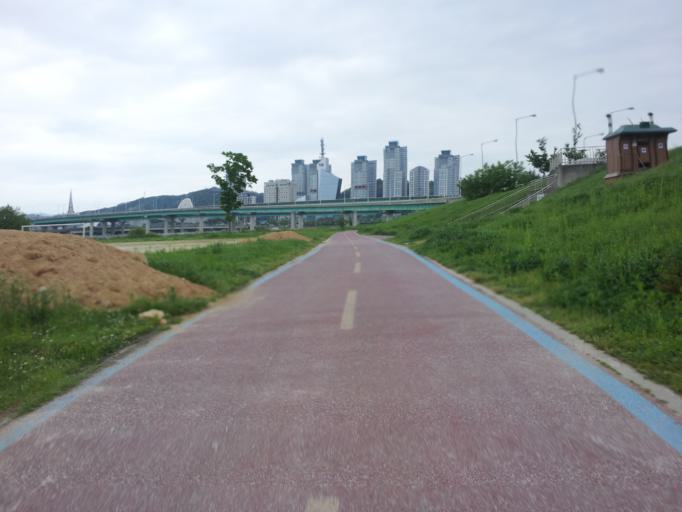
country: KR
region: Daejeon
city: Daejeon
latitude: 36.3680
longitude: 127.3969
